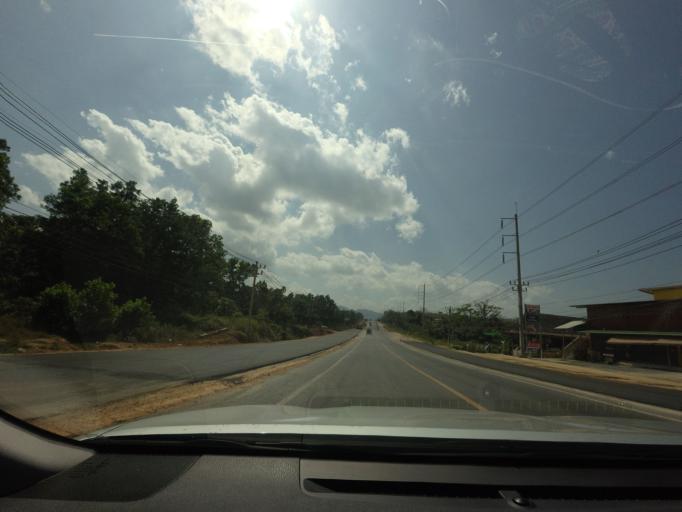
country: TH
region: Phangnga
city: Ban Khao Lak
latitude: 8.7203
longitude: 98.2571
